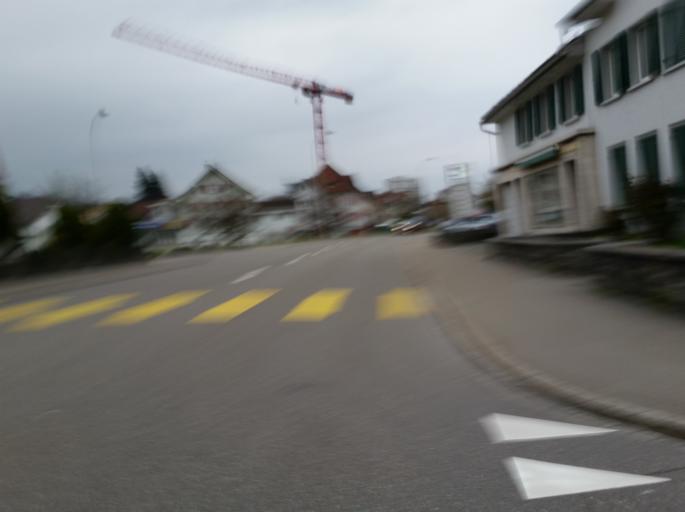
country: CH
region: Saint Gallen
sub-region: Wahlkreis Rheintal
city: Sankt Margrethen
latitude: 47.4496
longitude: 9.6375
